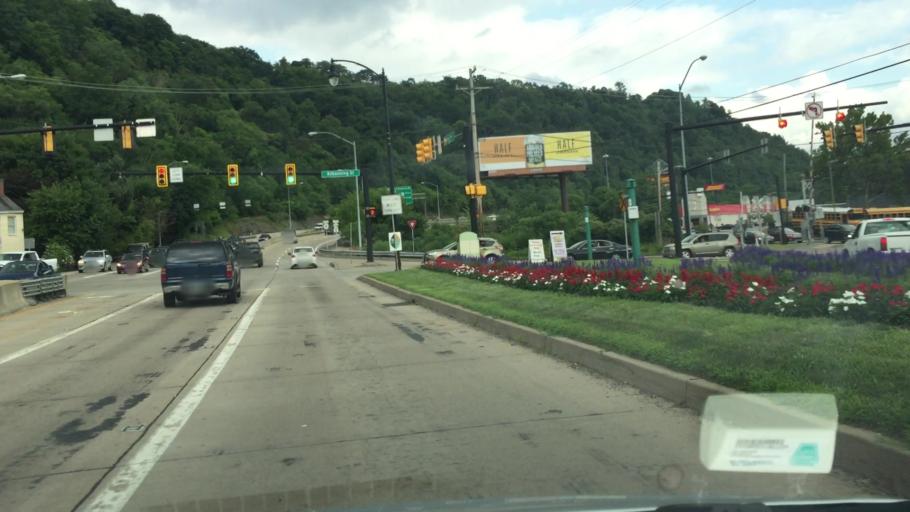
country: US
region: Pennsylvania
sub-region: Allegheny County
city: Etna
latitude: 40.5023
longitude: -79.9457
